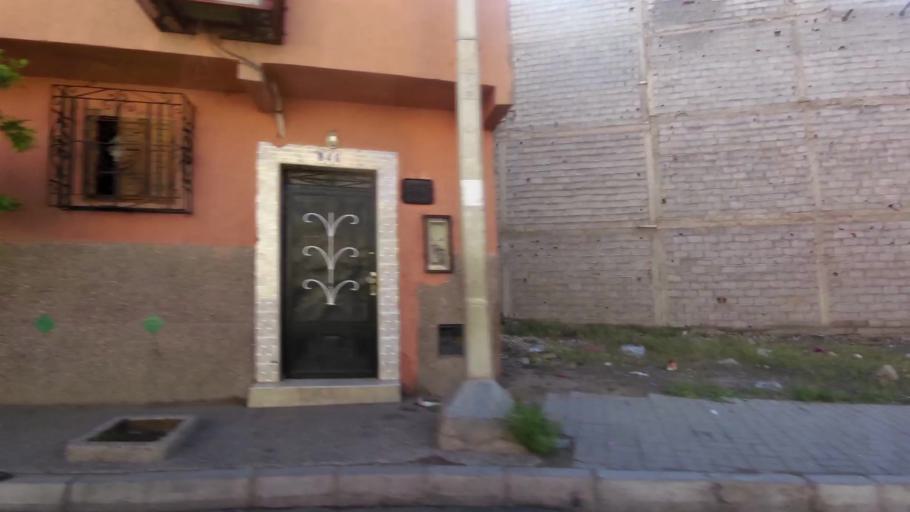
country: MA
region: Marrakech-Tensift-Al Haouz
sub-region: Marrakech
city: Marrakesh
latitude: 31.5982
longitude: -8.0301
